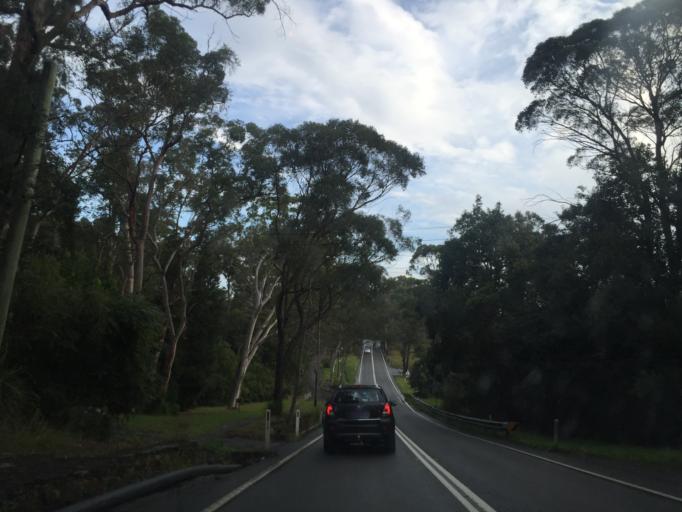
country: AU
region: New South Wales
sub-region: Hornsby Shire
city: Galston
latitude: -33.6634
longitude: 151.0388
